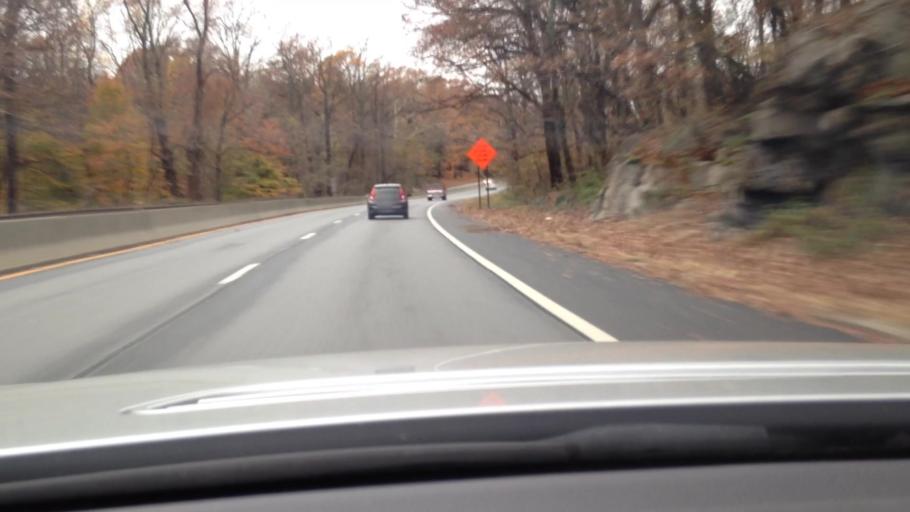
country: US
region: New York
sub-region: Westchester County
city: Elmsford
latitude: 41.0648
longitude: -73.8246
